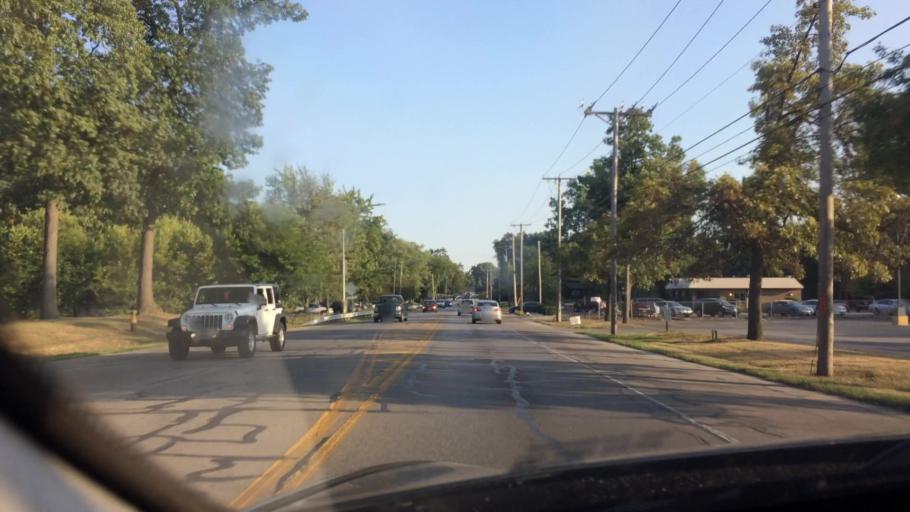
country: US
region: Ohio
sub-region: Lucas County
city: Holland
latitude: 41.6597
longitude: -83.7022
